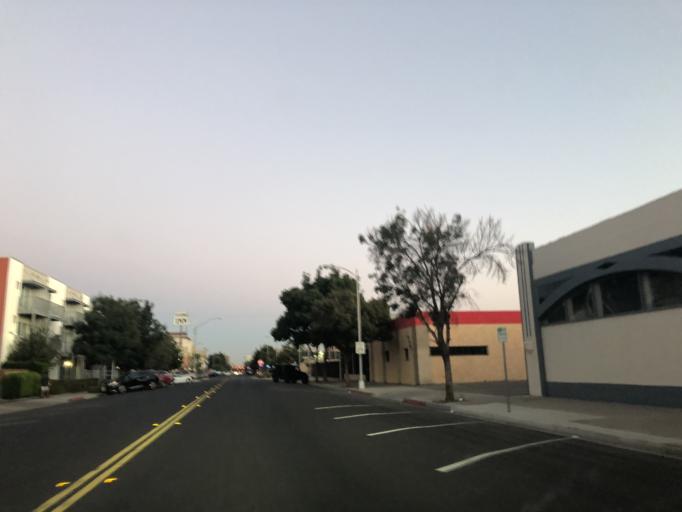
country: US
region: California
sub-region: Fresno County
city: Fresno
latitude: 36.7429
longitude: -119.8019
